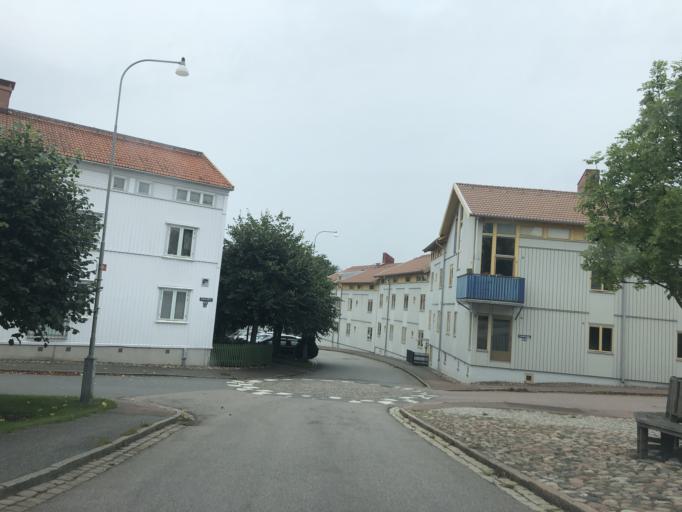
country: SE
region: Vaestra Goetaland
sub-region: Goteborg
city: Majorna
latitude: 57.7067
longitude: 11.9318
